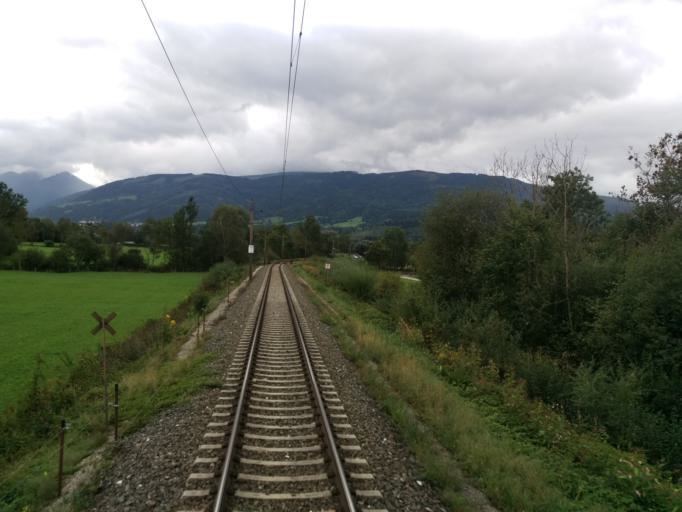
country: AT
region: Styria
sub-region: Politischer Bezirk Liezen
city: Irdning
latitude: 47.5210
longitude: 14.0851
